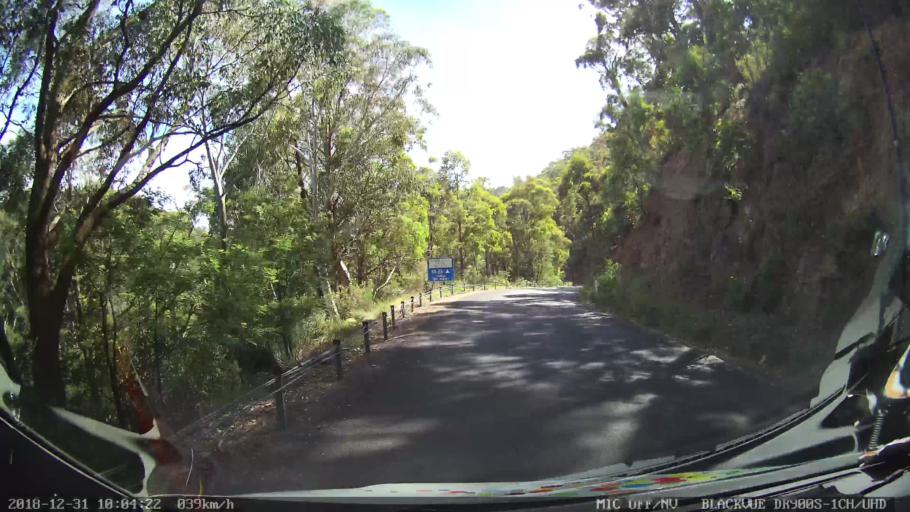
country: AU
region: New South Wales
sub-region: Snowy River
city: Jindabyne
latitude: -36.5317
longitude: 148.1909
